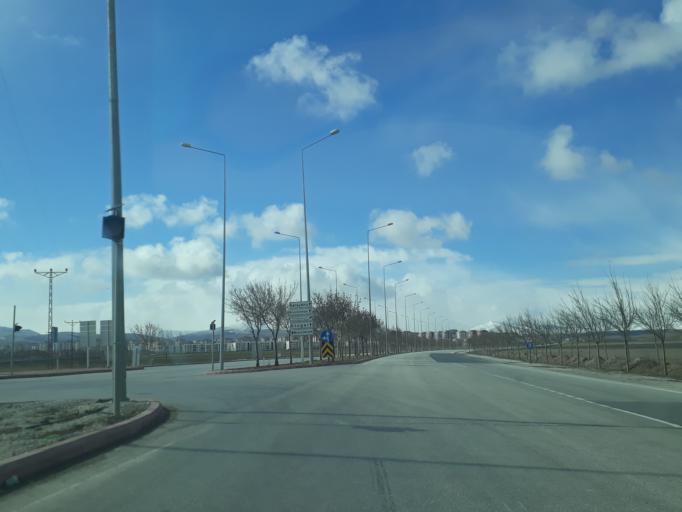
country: TR
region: Konya
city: Asagipinarbasi
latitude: 38.0056
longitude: 32.5534
